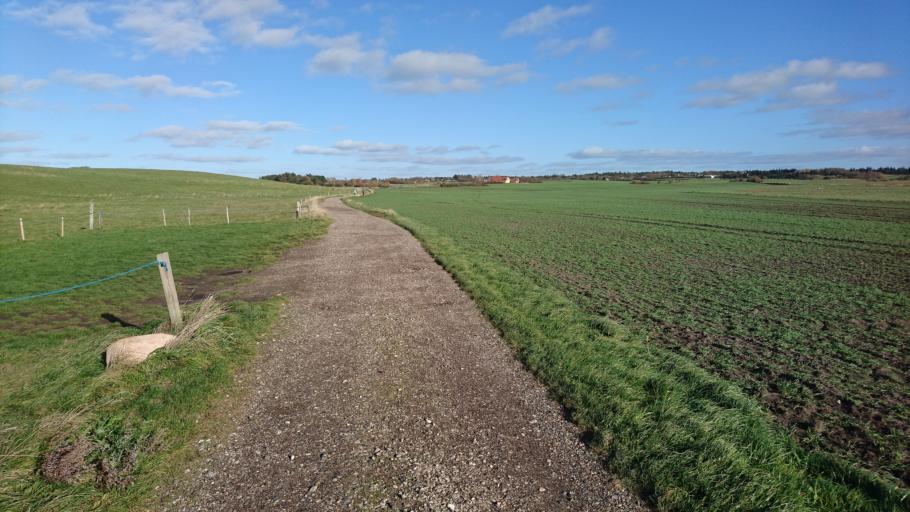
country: DK
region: North Denmark
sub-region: Vesthimmerland Kommune
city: Farso
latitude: 56.8062
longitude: 9.1697
